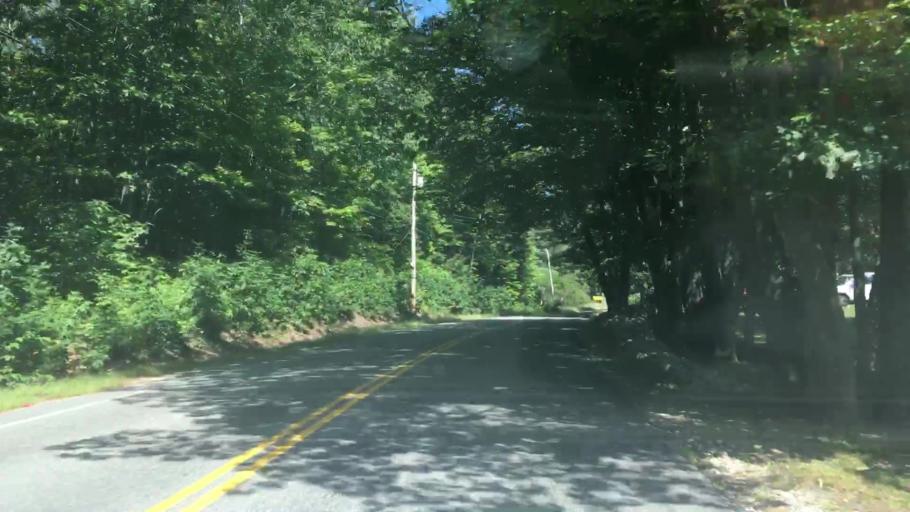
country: US
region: Maine
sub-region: Androscoggin County
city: Lisbon
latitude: 44.0618
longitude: -70.1182
